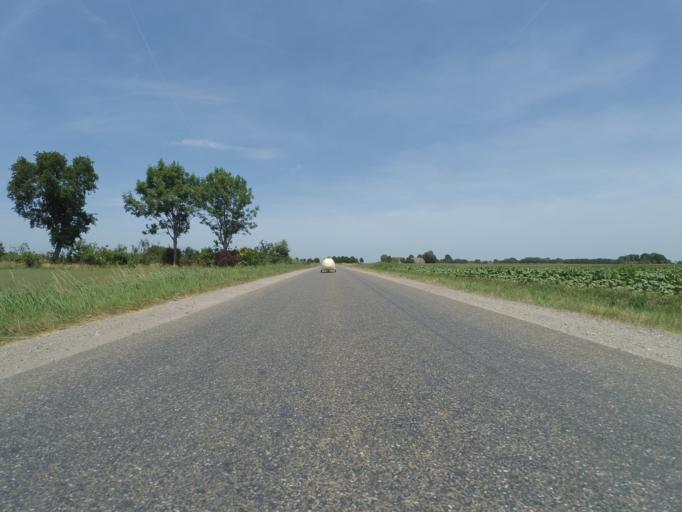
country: NL
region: North Brabant
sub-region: Gemeente Steenbergen
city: Welberg
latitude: 51.5385
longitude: 4.3591
